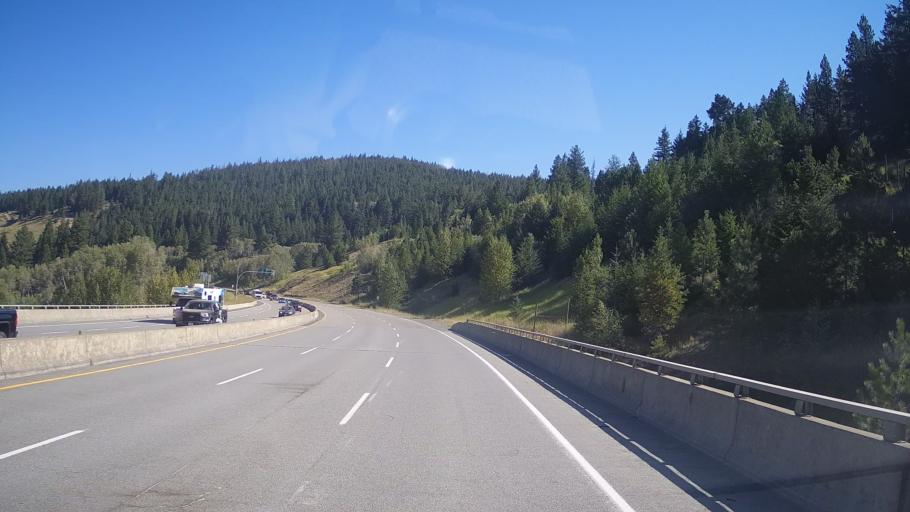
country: CA
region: British Columbia
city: Merritt
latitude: 49.8832
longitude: -120.9018
